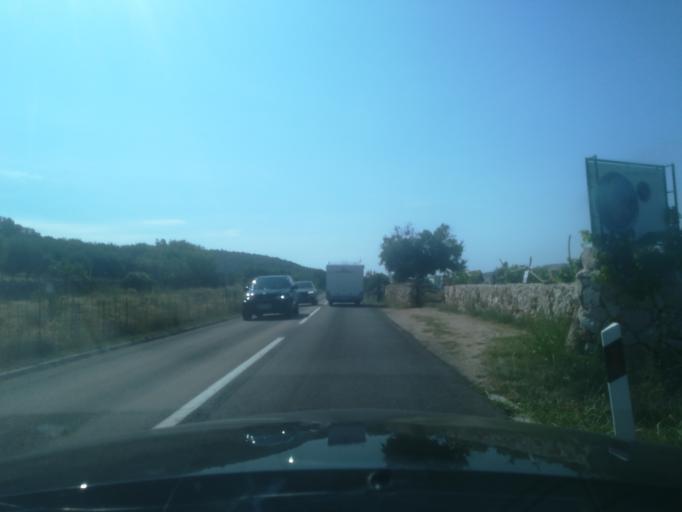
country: HR
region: Primorsko-Goranska
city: Banjol
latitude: 44.7227
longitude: 14.8211
